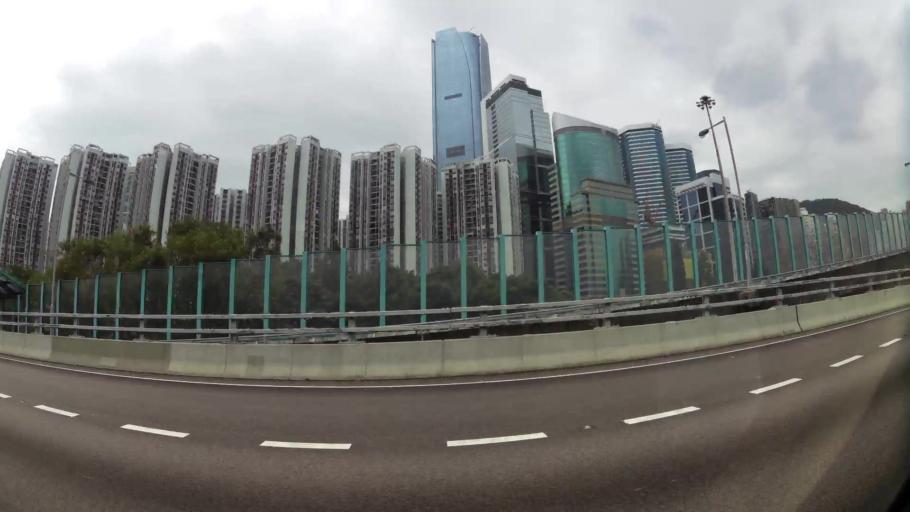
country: HK
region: Kowloon City
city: Kowloon
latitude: 22.2894
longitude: 114.2150
